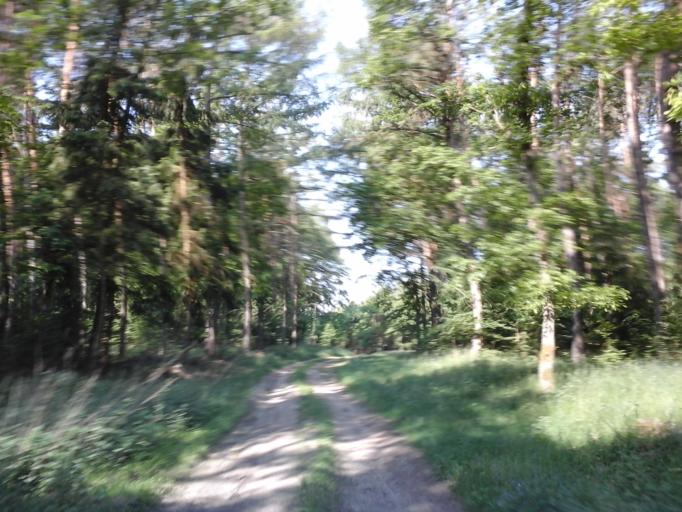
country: PL
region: West Pomeranian Voivodeship
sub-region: Powiat choszczenski
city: Recz
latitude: 53.3184
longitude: 15.5268
